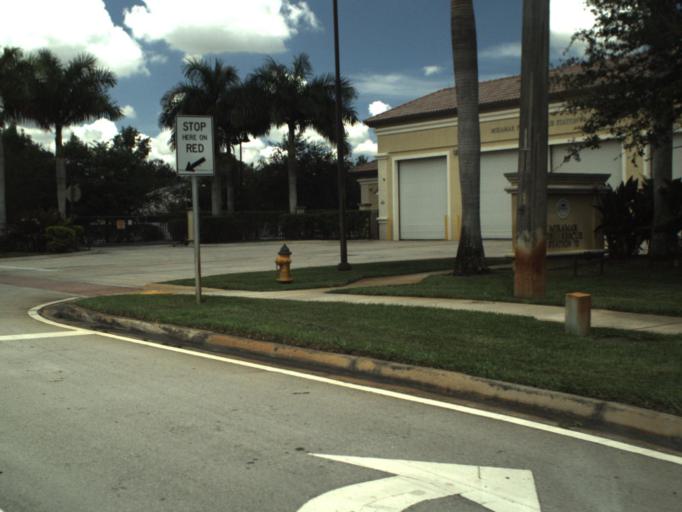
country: US
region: Florida
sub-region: Miami-Dade County
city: Lake Lucerne
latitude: 25.9810
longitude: -80.2673
